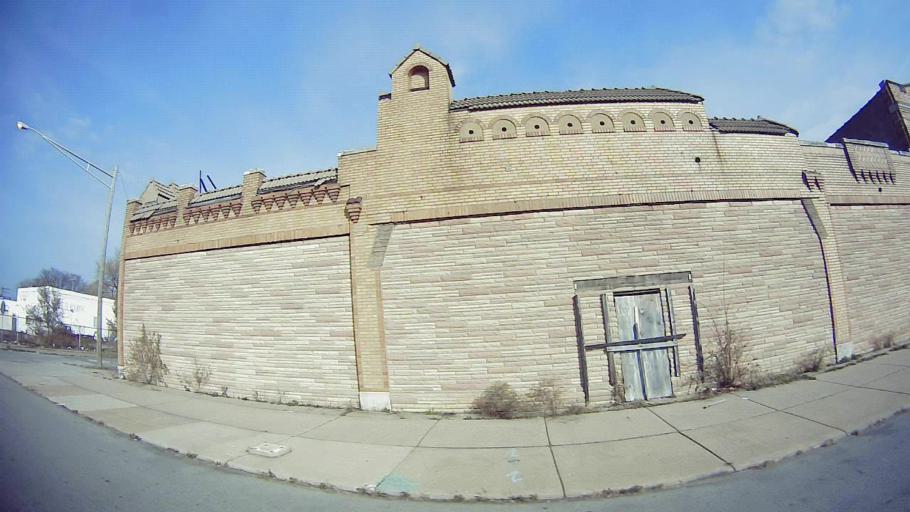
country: US
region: Michigan
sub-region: Wayne County
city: Highland Park
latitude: 42.4158
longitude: -83.1151
